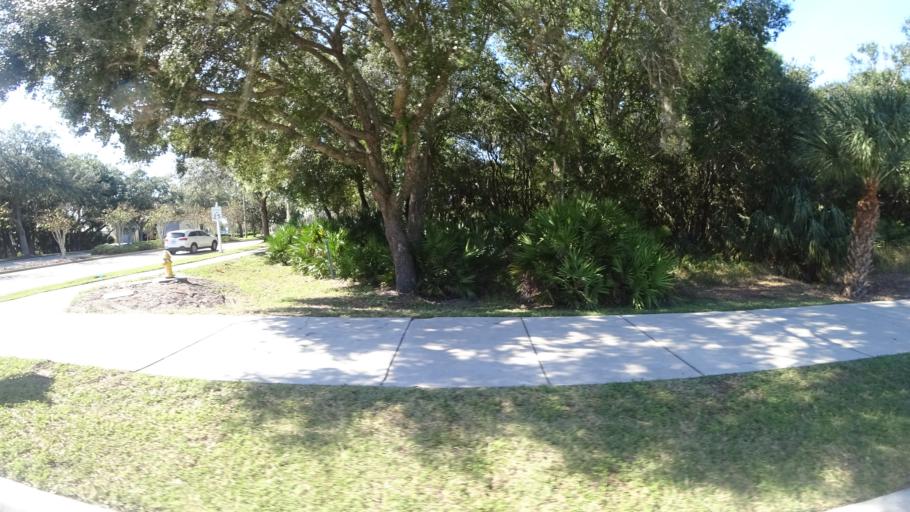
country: US
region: Florida
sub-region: Sarasota County
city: The Meadows
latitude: 27.3907
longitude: -82.4379
